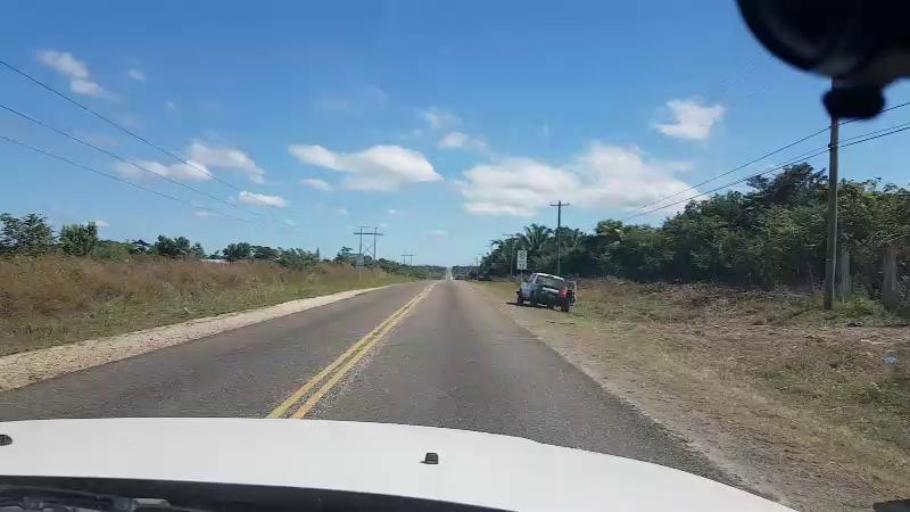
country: BZ
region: Cayo
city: Belmopan
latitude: 17.2768
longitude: -88.7309
